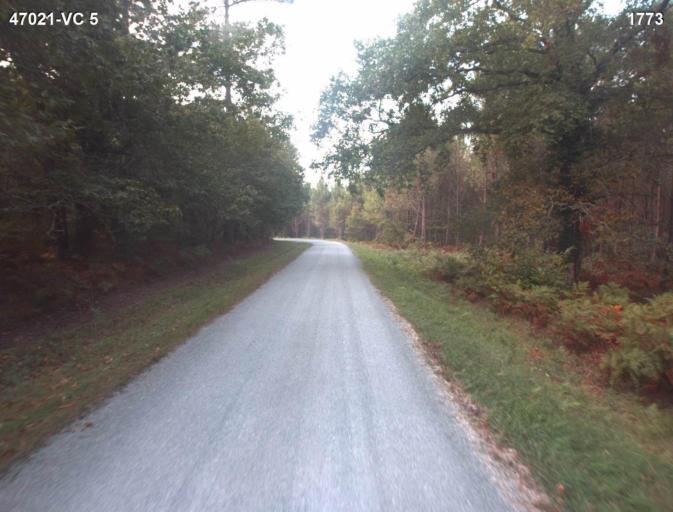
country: FR
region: Aquitaine
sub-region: Departement du Lot-et-Garonne
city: Barbaste
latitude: 44.1434
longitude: 0.2761
